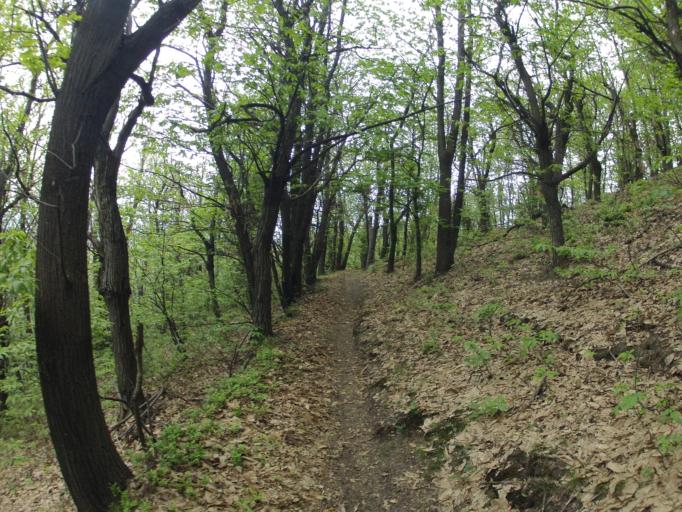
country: IT
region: Piedmont
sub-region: Provincia di Cuneo
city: Peveragno
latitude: 44.3216
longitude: 7.5864
